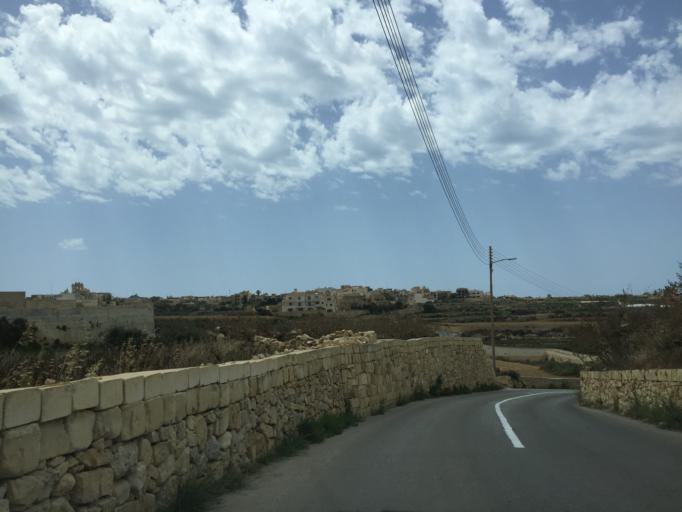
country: MT
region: L-Gharb
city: Gharb
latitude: 36.0627
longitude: 14.2156
